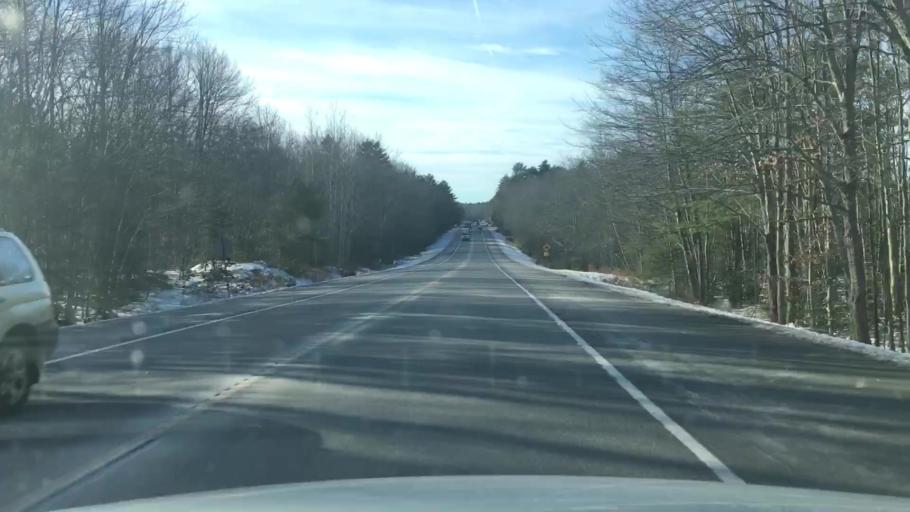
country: US
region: Maine
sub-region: Sagadahoc County
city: Woolwich
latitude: 43.9533
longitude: -69.7408
